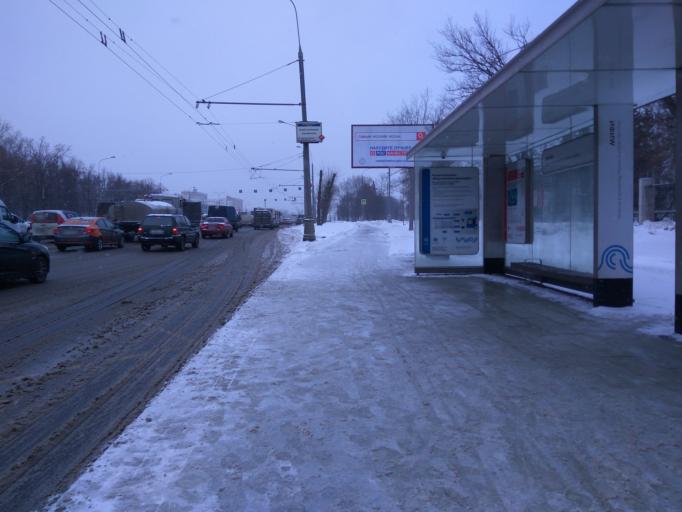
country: RU
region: Moscow
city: Kolomenskoye
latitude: 55.6497
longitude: 37.6623
